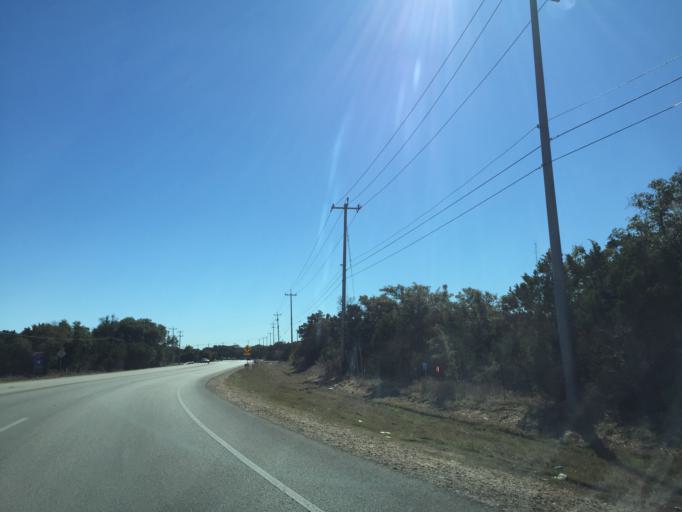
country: US
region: Texas
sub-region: Bexar County
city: Timberwood Park
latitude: 29.6929
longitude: -98.4503
